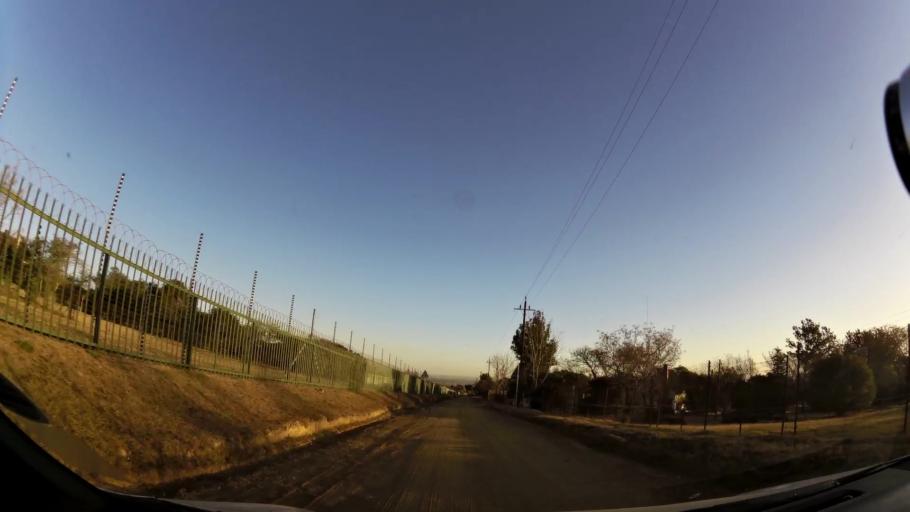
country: ZA
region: Gauteng
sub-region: City of Johannesburg Metropolitan Municipality
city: Diepsloot
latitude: -25.9404
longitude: 28.0412
